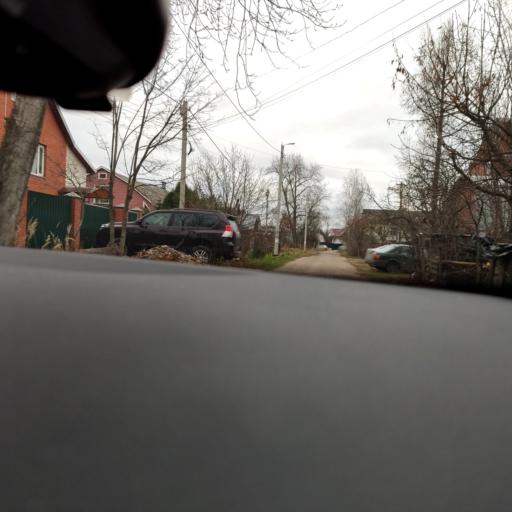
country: RU
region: Moskovskaya
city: Lobnya
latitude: 56.0086
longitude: 37.5032
